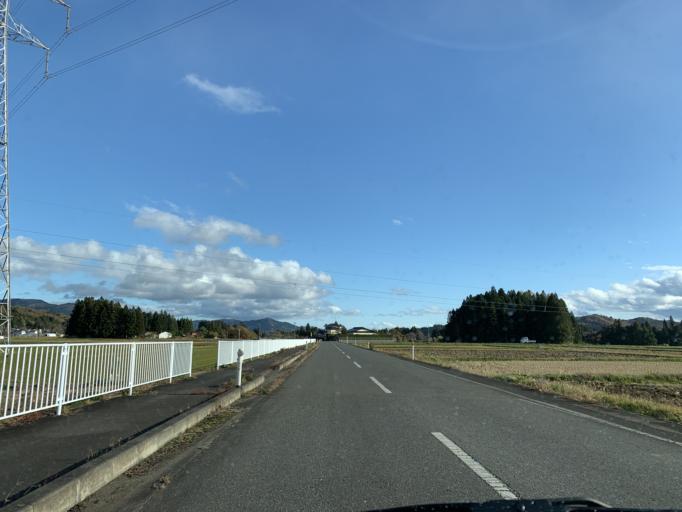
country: JP
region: Iwate
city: Ichinoseki
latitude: 39.0226
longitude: 141.0800
